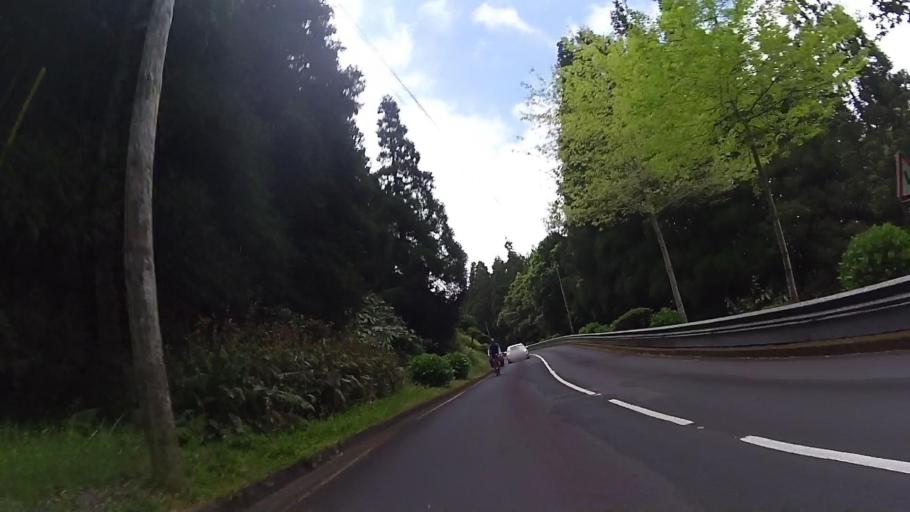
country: PT
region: Azores
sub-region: Povoacao
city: Furnas
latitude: 37.7649
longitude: -25.2884
